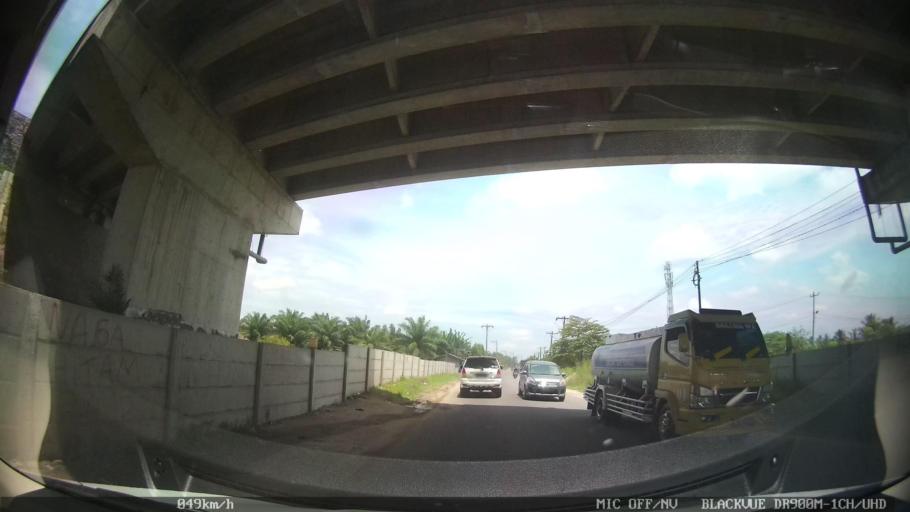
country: ID
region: North Sumatra
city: Perbaungan
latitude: 3.5315
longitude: 98.8865
